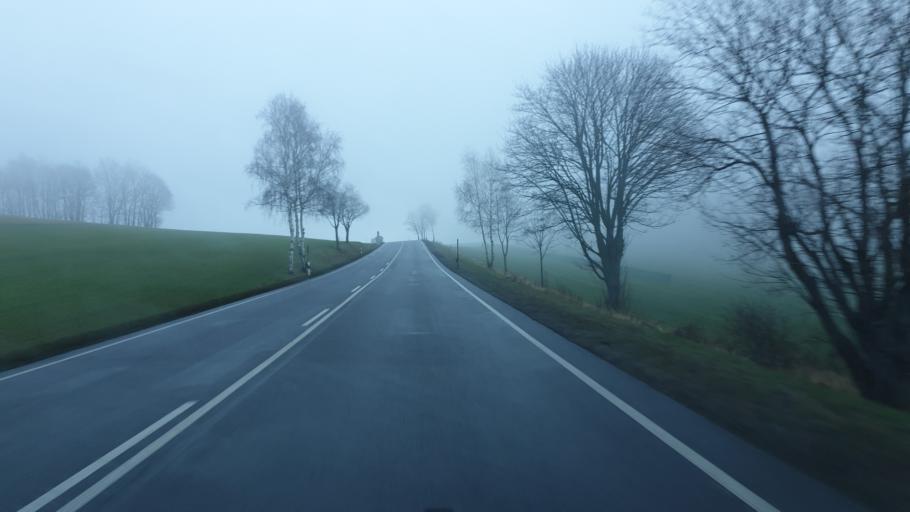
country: DE
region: Saxony
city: Grossolbersdorf
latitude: 50.6964
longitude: 13.1114
